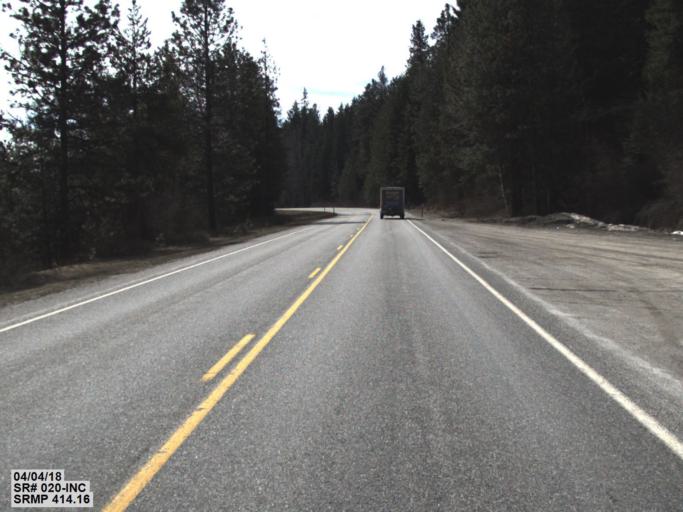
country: US
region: Washington
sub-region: Pend Oreille County
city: Newport
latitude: 48.4064
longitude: -117.3140
